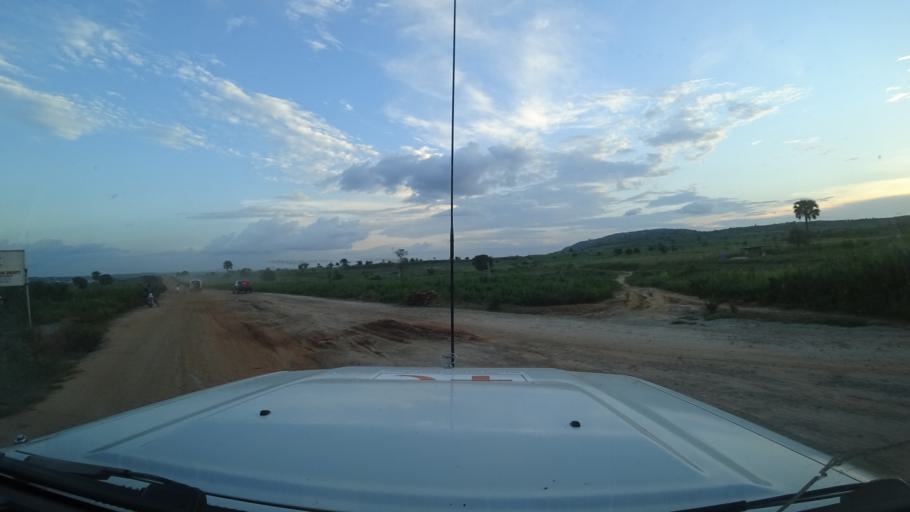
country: NG
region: Niger
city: Minna
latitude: 9.6566
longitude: 6.5748
